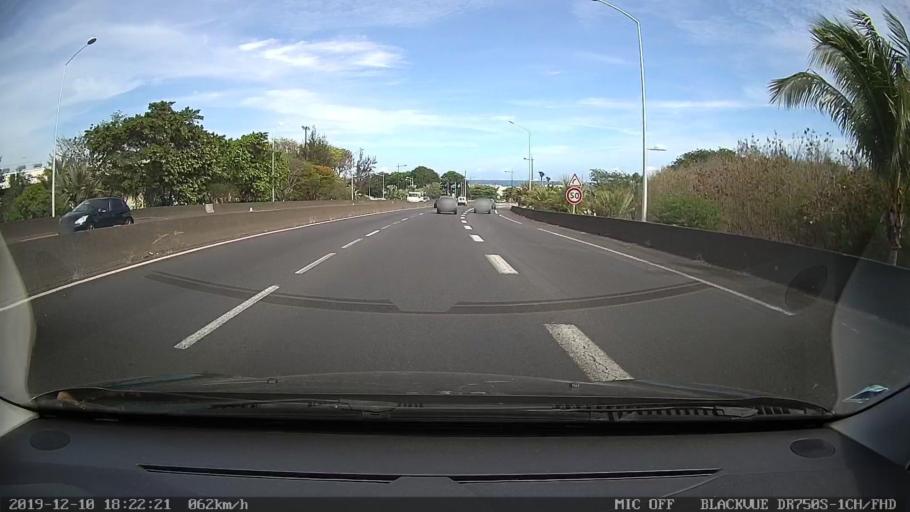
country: RE
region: Reunion
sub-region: Reunion
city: Sainte-Marie
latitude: -20.8950
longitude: 55.5039
